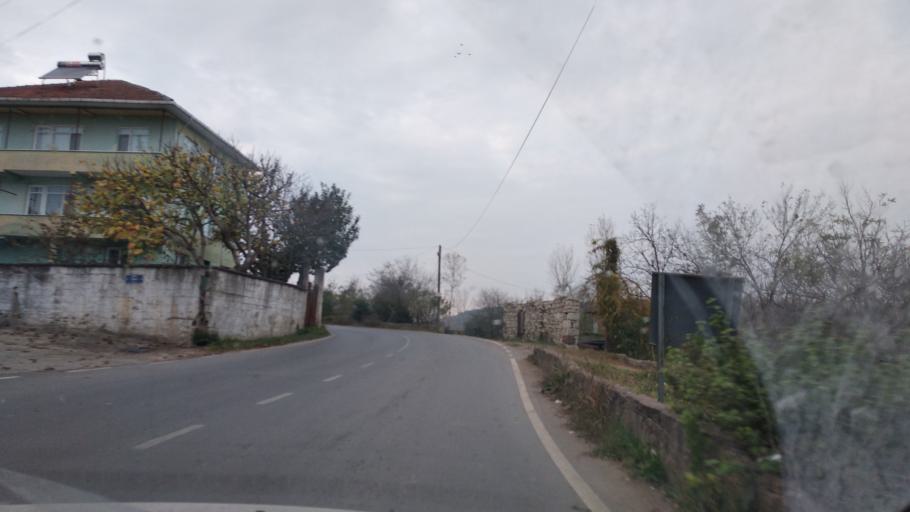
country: TR
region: Sakarya
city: Ortakoy
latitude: 41.0386
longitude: 30.6432
